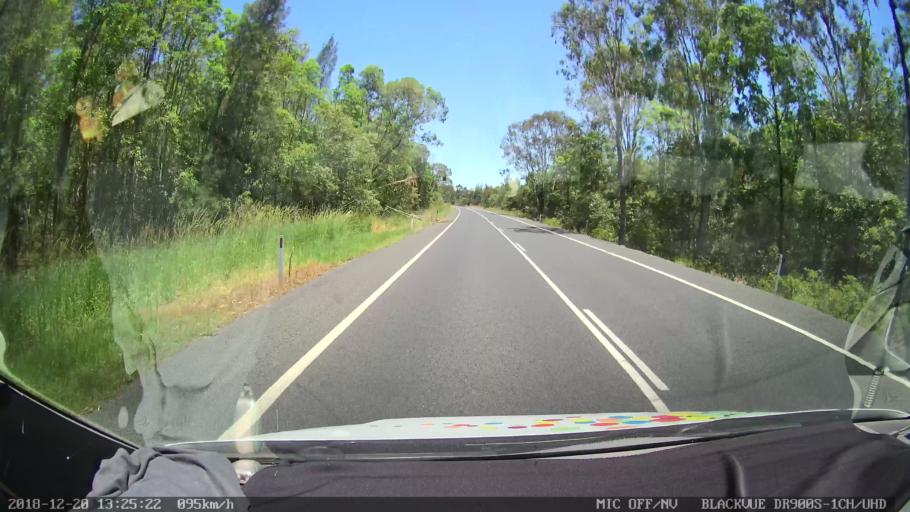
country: AU
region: New South Wales
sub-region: Richmond Valley
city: Casino
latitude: -29.1303
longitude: 152.9966
